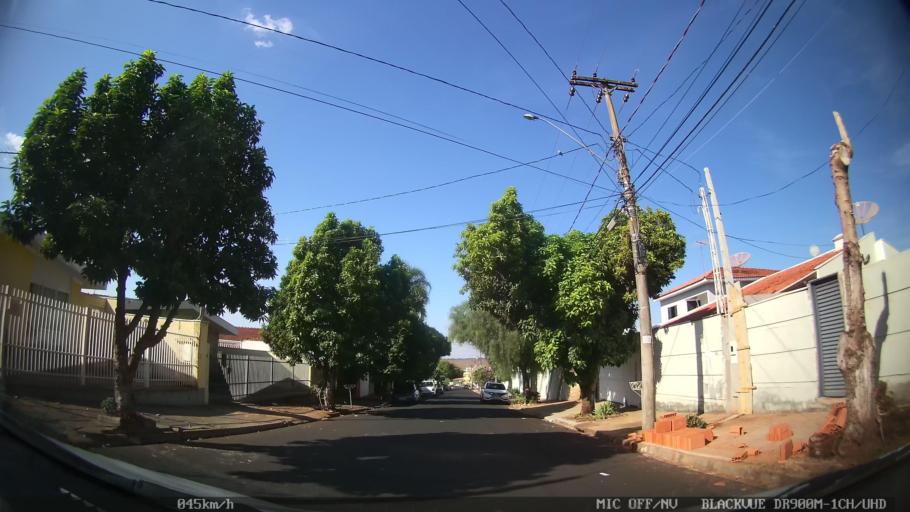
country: BR
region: Sao Paulo
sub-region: Ribeirao Preto
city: Ribeirao Preto
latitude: -21.1753
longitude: -47.7640
